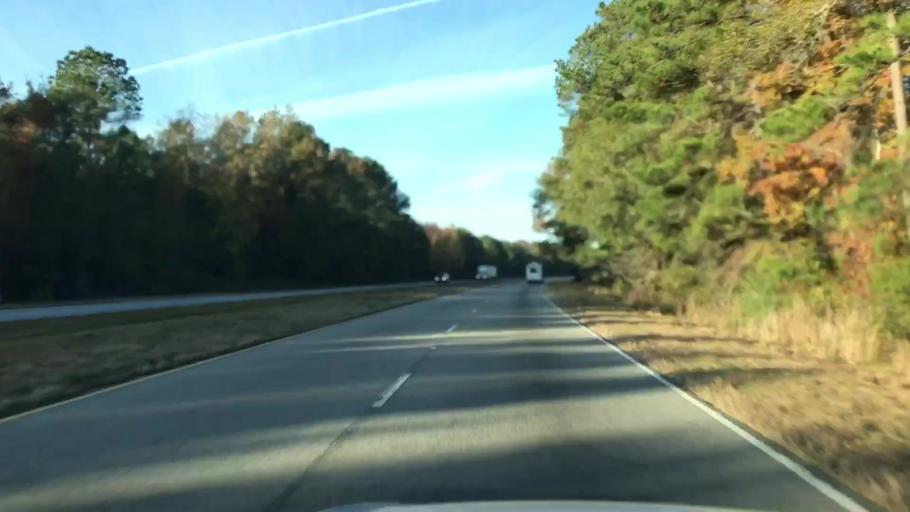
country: US
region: South Carolina
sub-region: Charleston County
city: Ravenel
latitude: 32.7555
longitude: -80.3285
